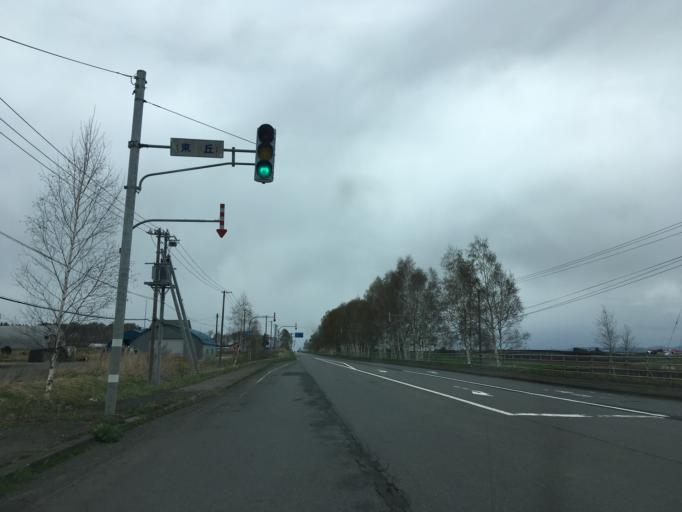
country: JP
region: Hokkaido
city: Chitose
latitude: 42.9154
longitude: 141.8102
